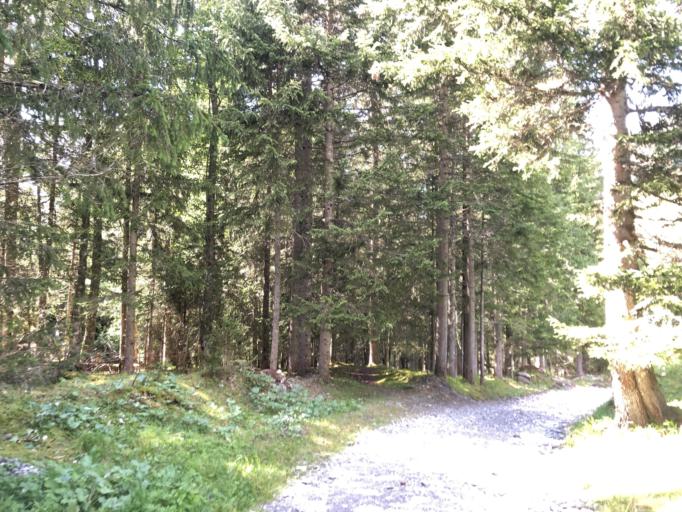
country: FR
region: Rhone-Alpes
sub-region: Departement de la Haute-Savoie
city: Megeve
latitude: 45.8297
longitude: 6.6626
